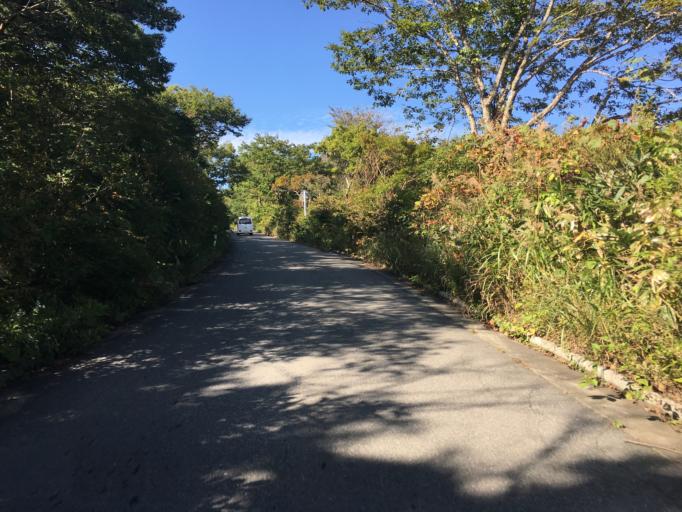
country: JP
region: Yamagata
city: Yonezawa
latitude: 37.8104
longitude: 140.2534
